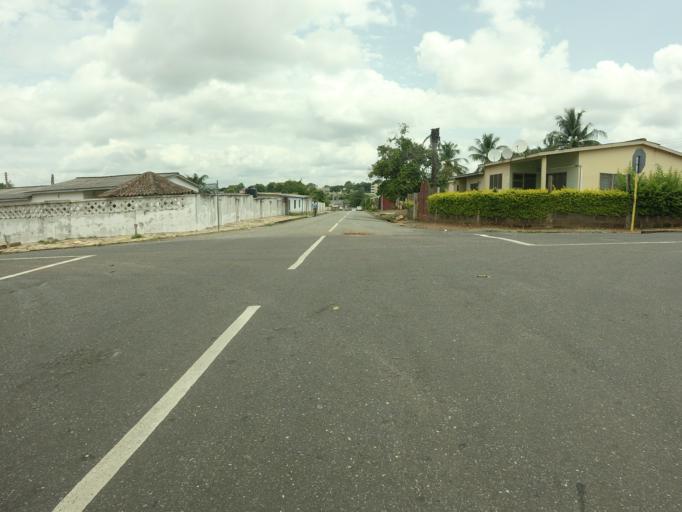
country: GH
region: Volta
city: Ho
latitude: 6.5921
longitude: 0.4743
